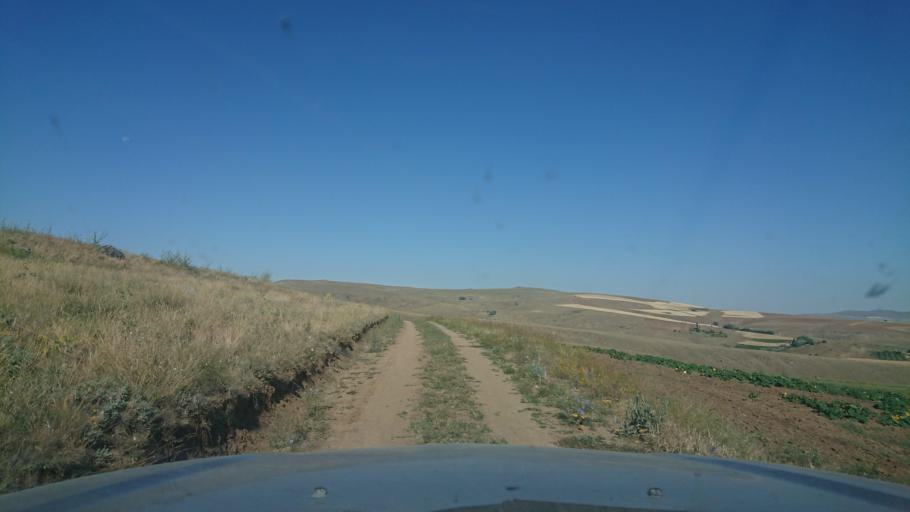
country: TR
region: Aksaray
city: Agacoren
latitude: 38.8353
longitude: 33.9323
